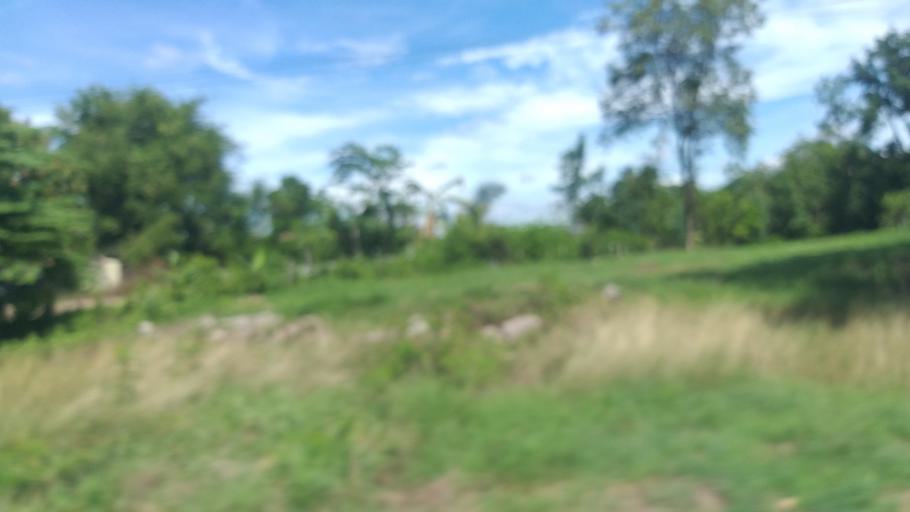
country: TH
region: Khon Kaen
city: Nong Ruea
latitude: 16.4707
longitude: 102.4416
